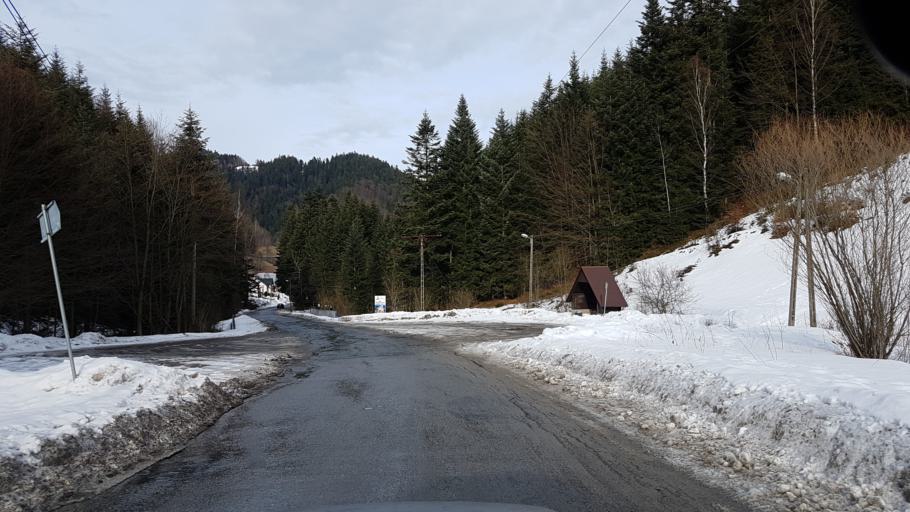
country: PL
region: Lesser Poland Voivodeship
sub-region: Powiat nowosadecki
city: Piwniczna-Zdroj
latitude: 49.4208
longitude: 20.6491
